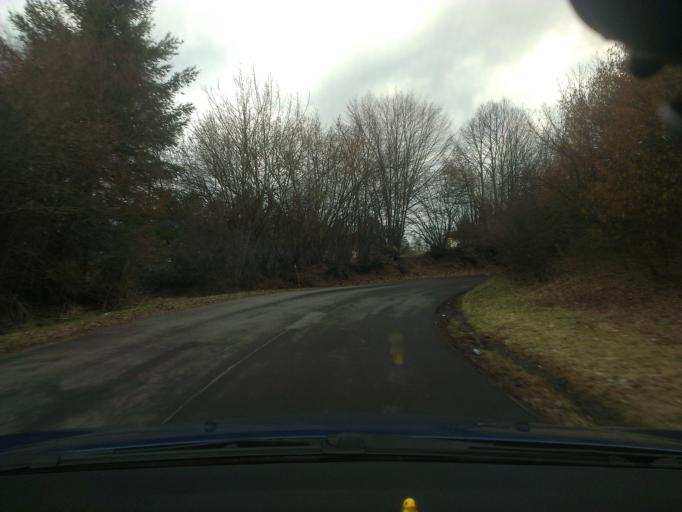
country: SK
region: Banskobystricky
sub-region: Okres Banska Bystrica
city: Banska Stiavnica
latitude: 48.4515
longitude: 18.9276
